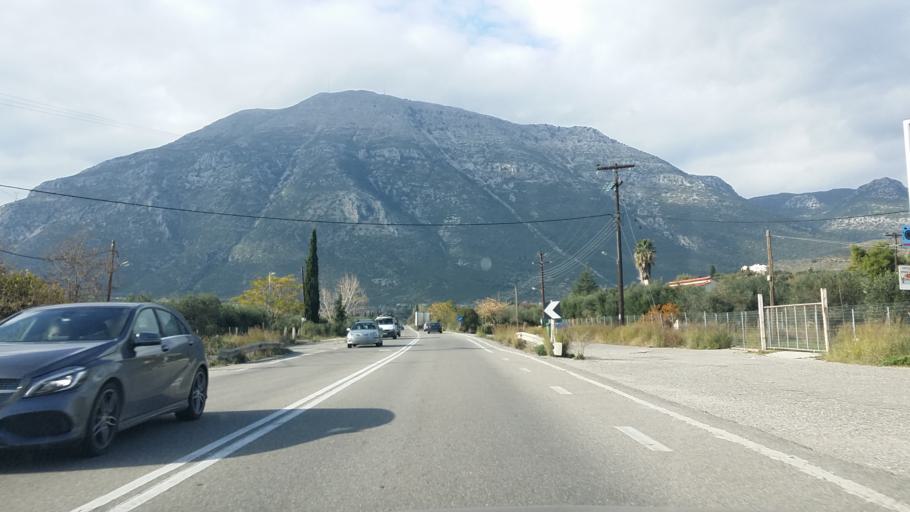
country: GR
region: West Greece
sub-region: Nomos Aitolias kai Akarnanias
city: Antirrio
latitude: 38.3475
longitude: 21.7191
